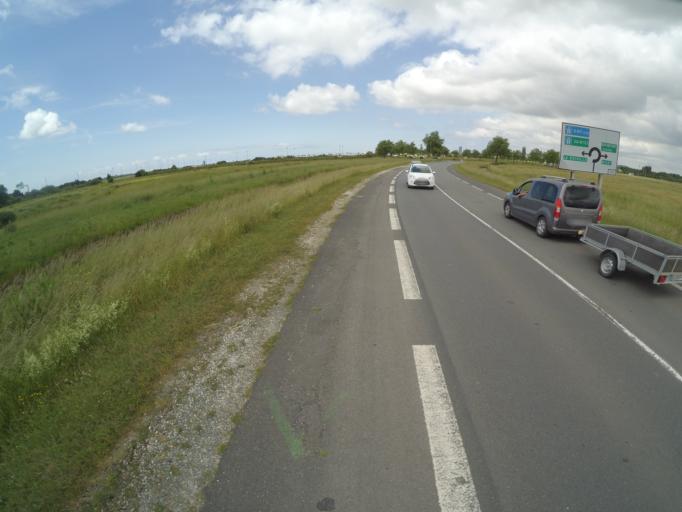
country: FR
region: Poitou-Charentes
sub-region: Departement de la Charente-Maritime
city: Rochefort
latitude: 45.9220
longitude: -0.9682
